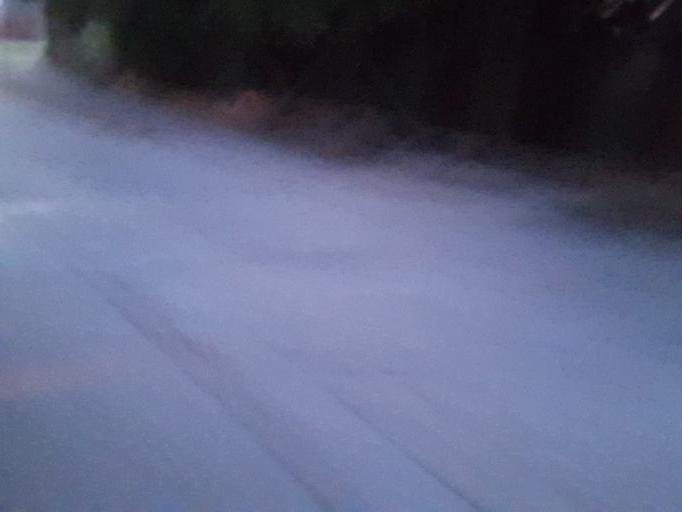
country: CO
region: Quindio
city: Armenia
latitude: 4.5195
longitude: -75.6907
